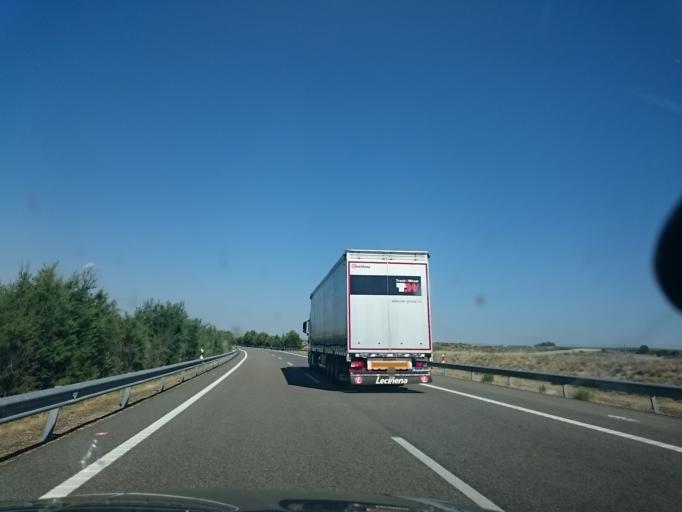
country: ES
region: Aragon
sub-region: Provincia de Huesca
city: Penalba
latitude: 41.5124
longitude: -0.0687
